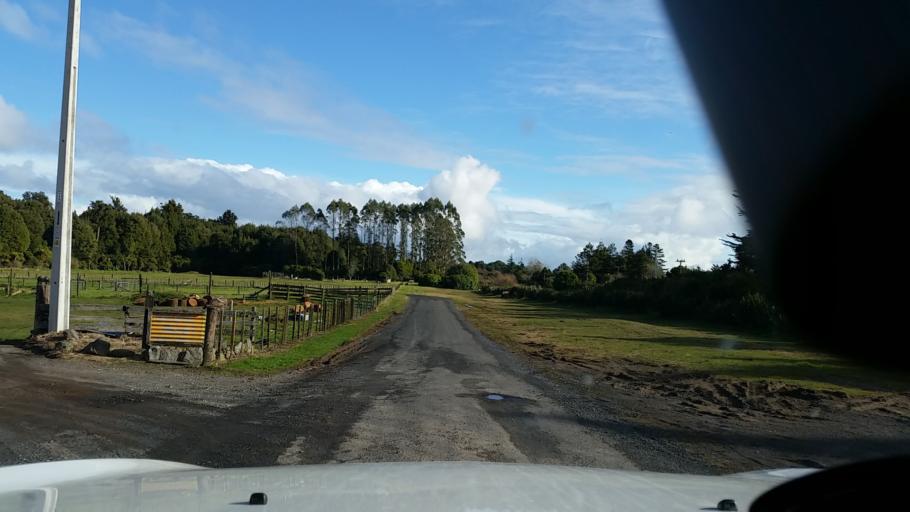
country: NZ
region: Bay of Plenty
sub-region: Rotorua District
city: Rotorua
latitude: -38.0975
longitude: 176.0750
